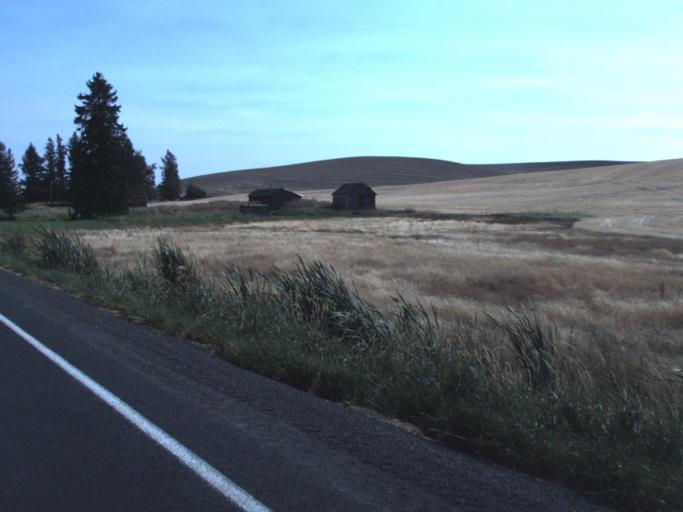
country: US
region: Idaho
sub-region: Benewah County
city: Plummer
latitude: 47.1957
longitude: -117.1332
